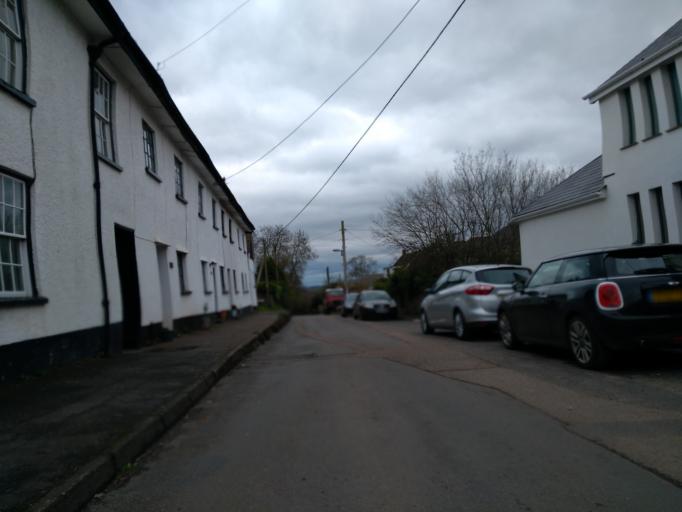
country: GB
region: England
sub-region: Devon
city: Bradninch
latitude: 50.8154
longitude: -3.4838
